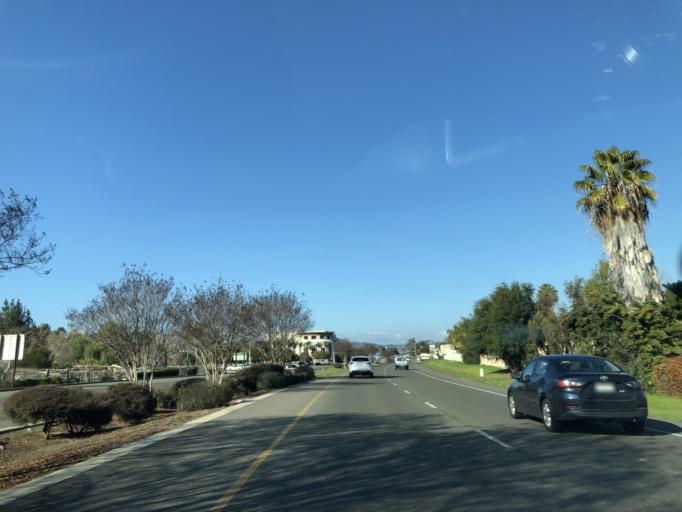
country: US
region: California
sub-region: San Diego County
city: Escondido
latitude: 33.1327
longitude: -117.0932
